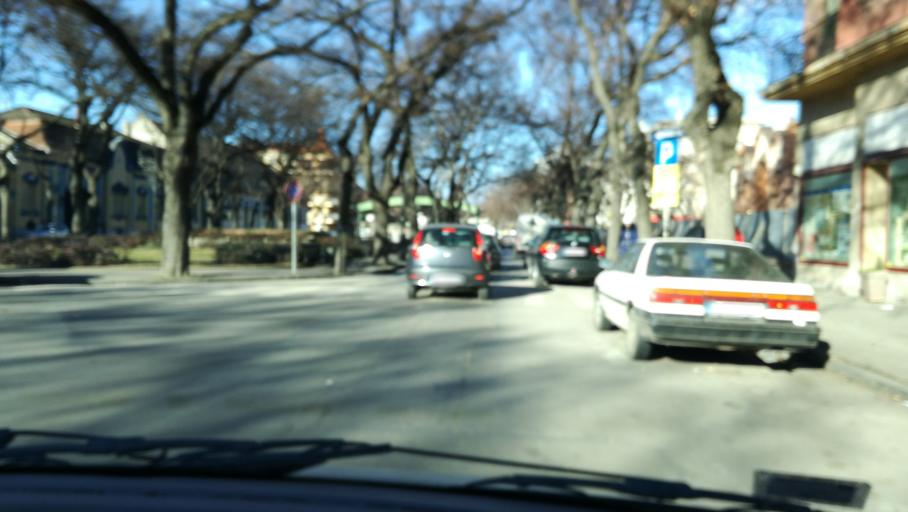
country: RS
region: Autonomna Pokrajina Vojvodina
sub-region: Severnobacki Okrug
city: Subotica
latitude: 46.1009
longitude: 19.6613
